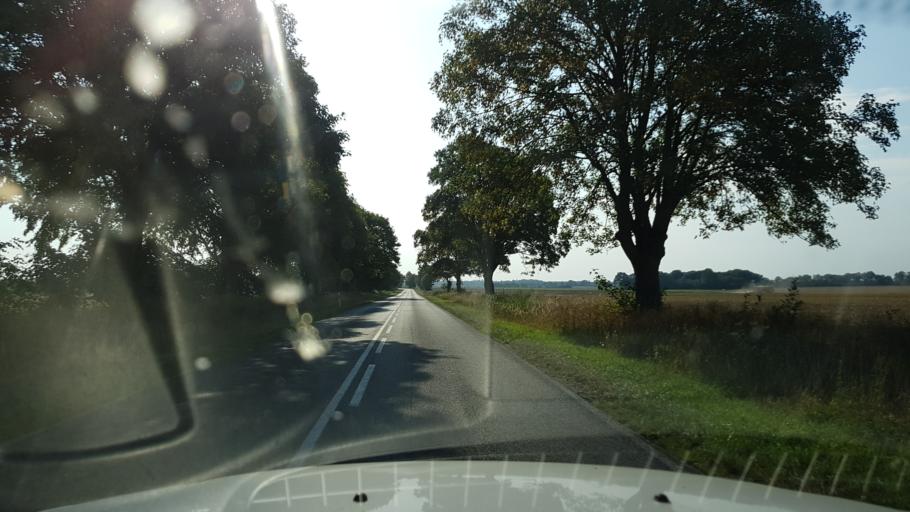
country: PL
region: West Pomeranian Voivodeship
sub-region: Powiat gryficki
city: Ploty
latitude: 53.7954
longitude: 15.2800
